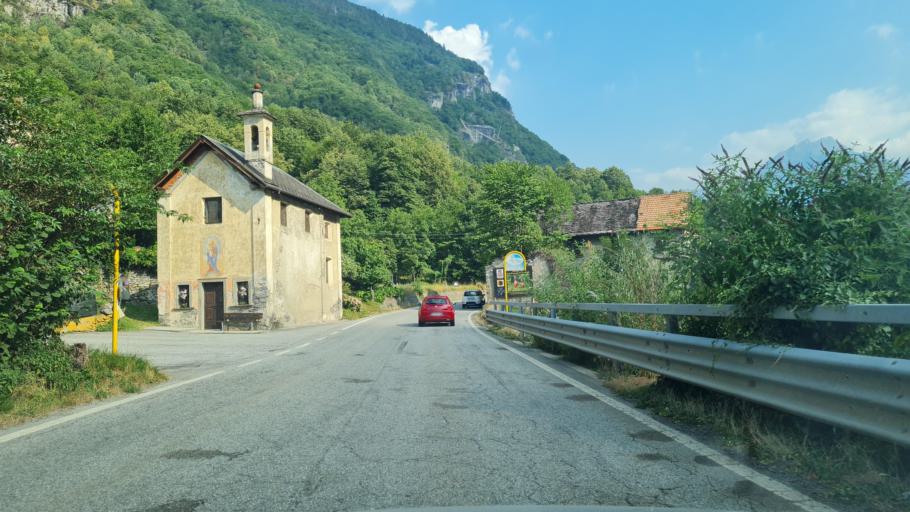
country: IT
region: Piedmont
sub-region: Provincia Verbano-Cusio-Ossola
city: Crodo
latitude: 46.1959
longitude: 8.3186
